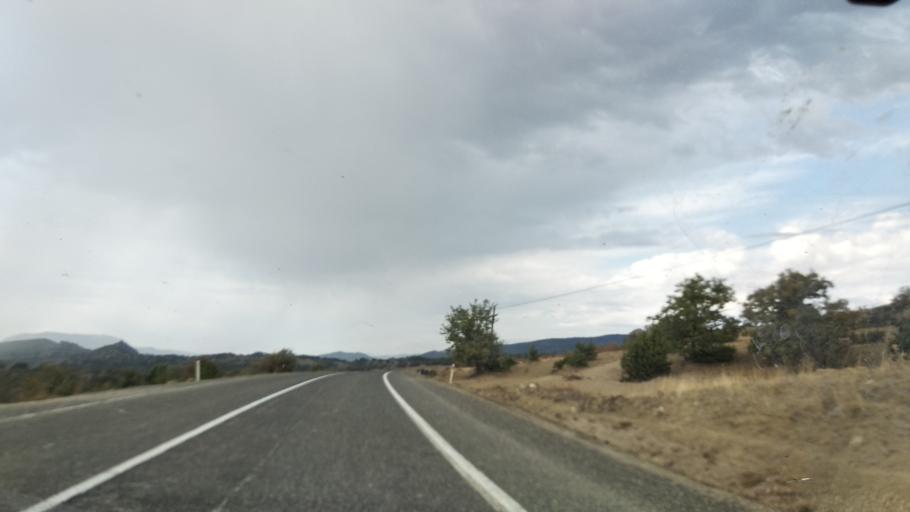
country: TR
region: Bolu
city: Seben
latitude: 40.3326
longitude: 31.4598
